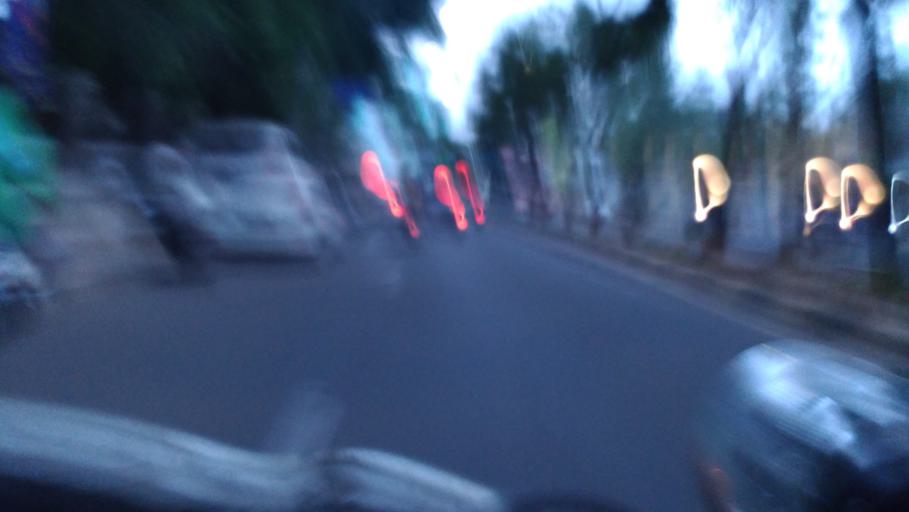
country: ID
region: West Java
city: Cileungsir
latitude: -6.3696
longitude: 106.8923
